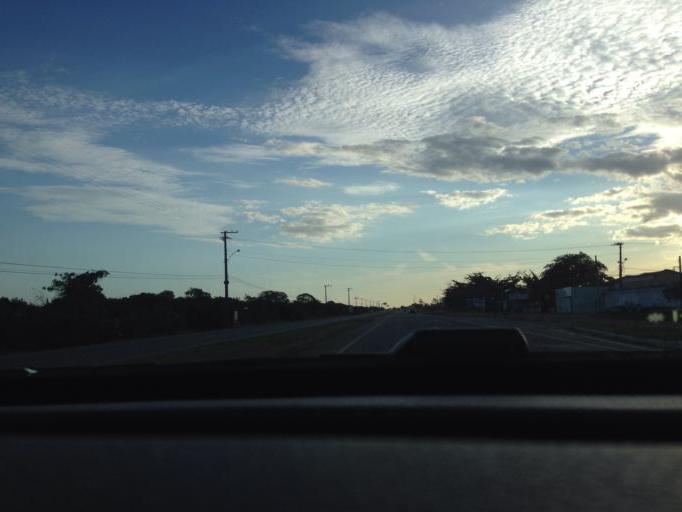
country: BR
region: Espirito Santo
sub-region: Guarapari
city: Guarapari
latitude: -20.5534
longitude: -40.4013
